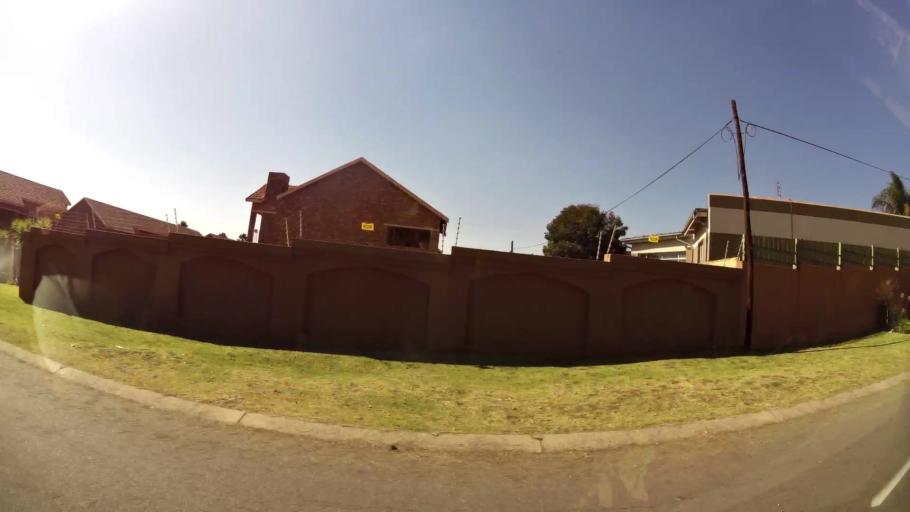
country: ZA
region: Gauteng
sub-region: City of Johannesburg Metropolitan Municipality
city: Modderfontein
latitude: -26.0678
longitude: 28.1977
